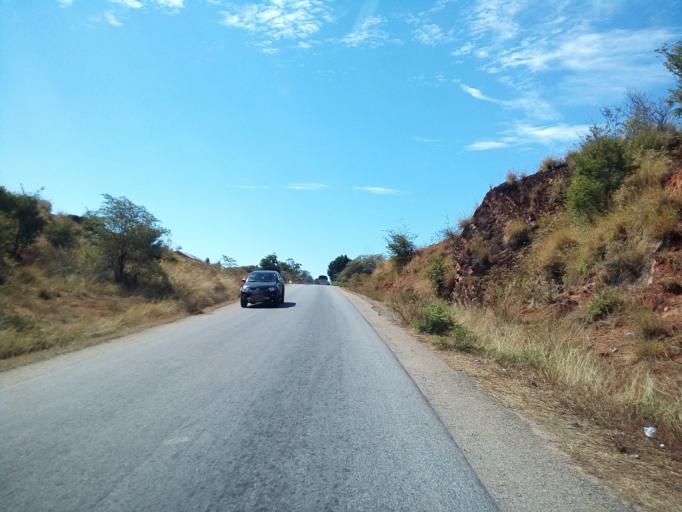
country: MG
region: Betsiboka
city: Maevatanana
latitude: -16.9214
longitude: 46.8665
